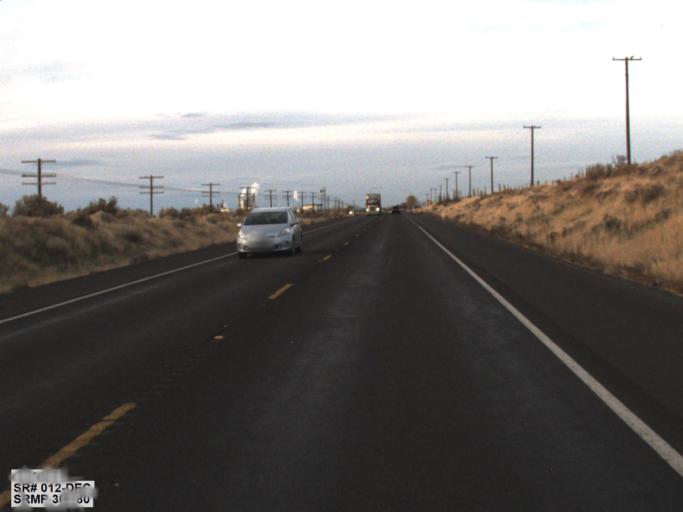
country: US
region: Washington
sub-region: Benton County
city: Finley
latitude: 46.0820
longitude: -118.9087
